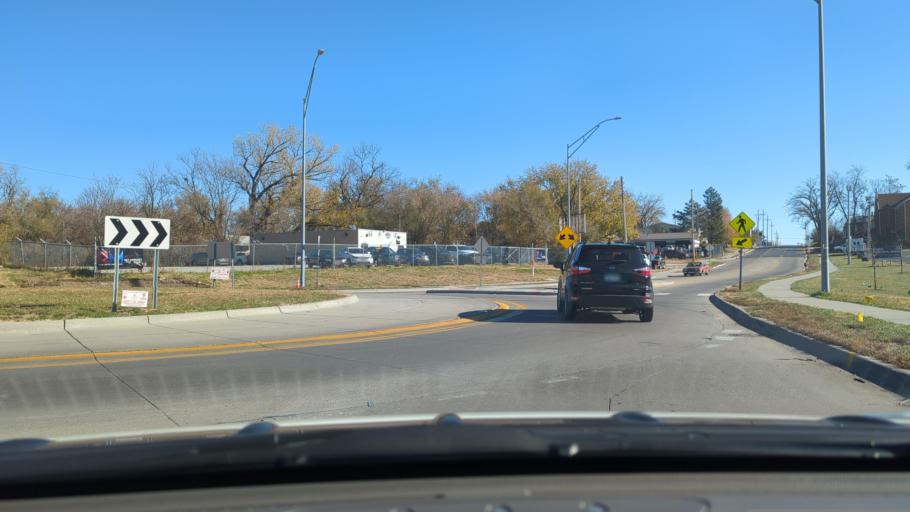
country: US
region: Nebraska
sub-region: Sarpy County
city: La Vista
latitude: 41.2053
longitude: -95.9765
